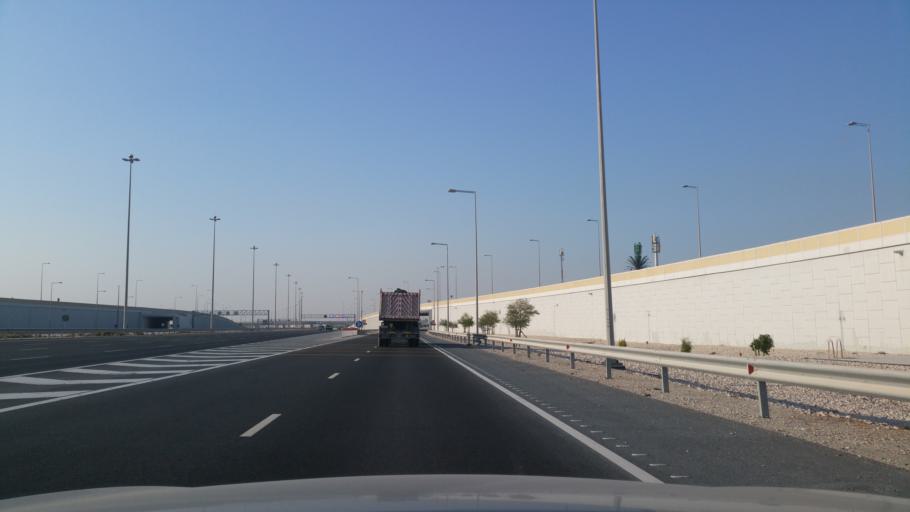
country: QA
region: Al Wakrah
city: Al Wakrah
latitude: 25.1527
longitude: 51.5746
